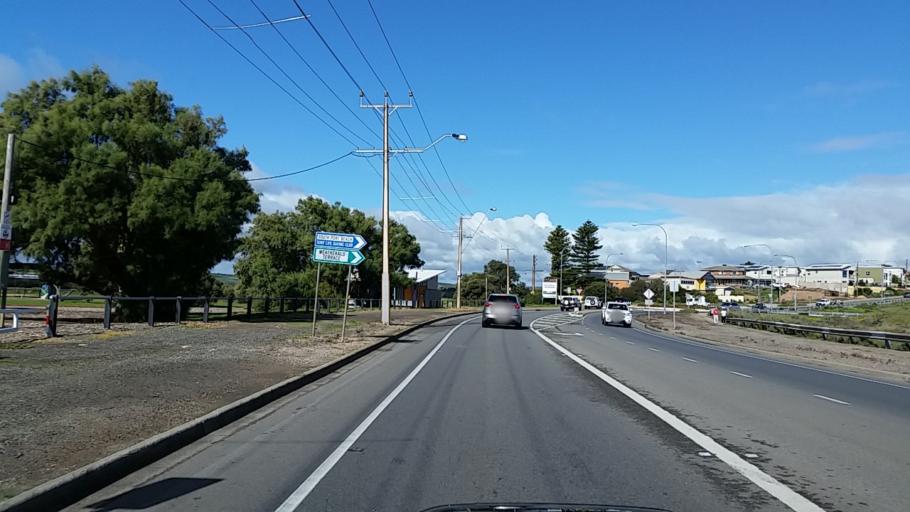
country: AU
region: South Australia
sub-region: Adelaide
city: Port Noarlunga
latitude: -35.1539
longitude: 138.4745
